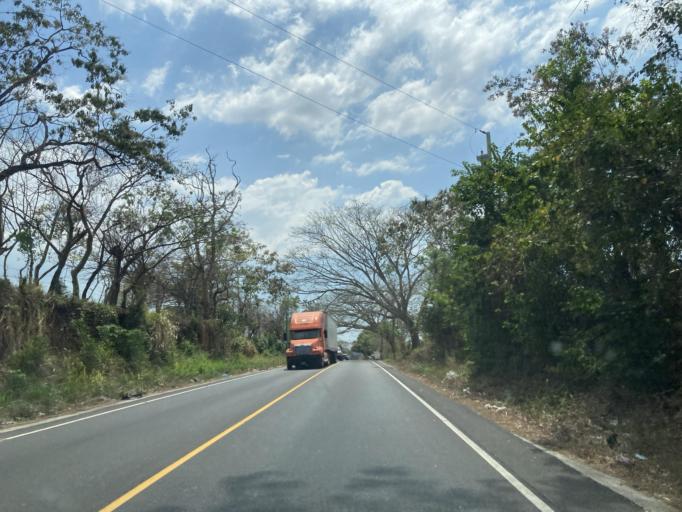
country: GT
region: Santa Rosa
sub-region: Municipio de Taxisco
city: Taxisco
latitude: 14.0736
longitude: -90.4756
